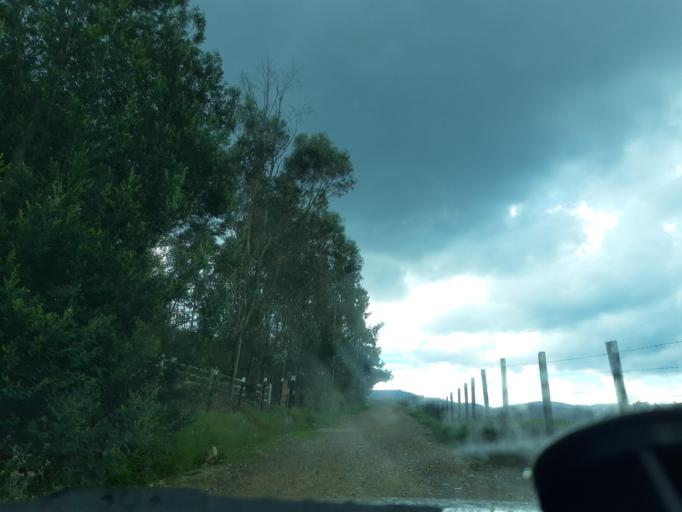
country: CO
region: Boyaca
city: Raquira
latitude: 5.4929
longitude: -73.7015
